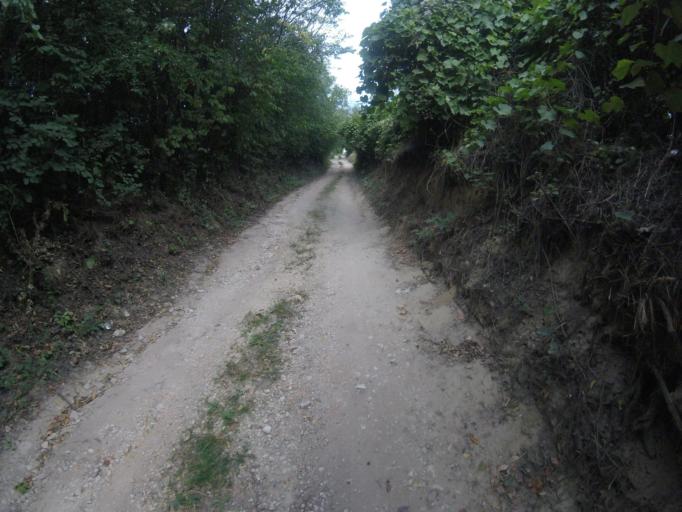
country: HU
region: Pest
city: Perbal
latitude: 47.5741
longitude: 18.7358
